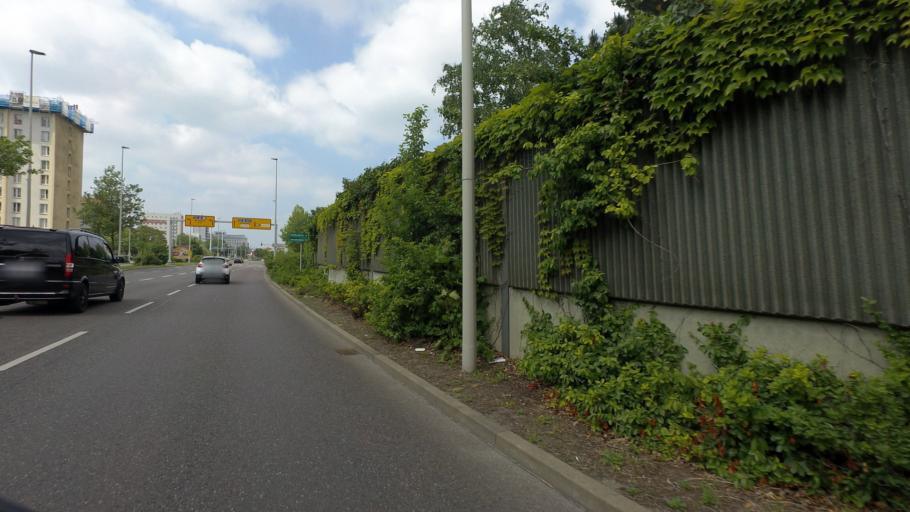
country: DE
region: Brandenburg
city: Cottbus
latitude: 51.7489
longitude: 14.3351
